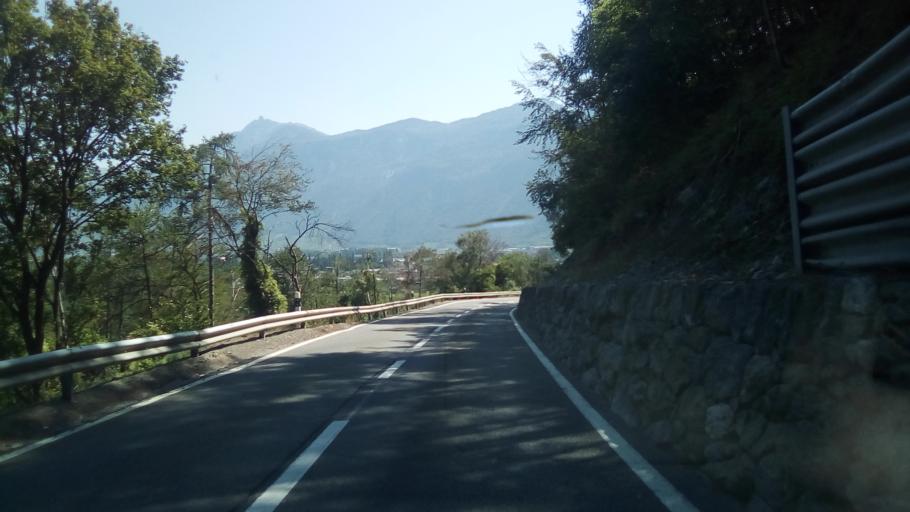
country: CH
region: Valais
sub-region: Martigny District
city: Martigny-Ville
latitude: 46.1129
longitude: 7.0535
